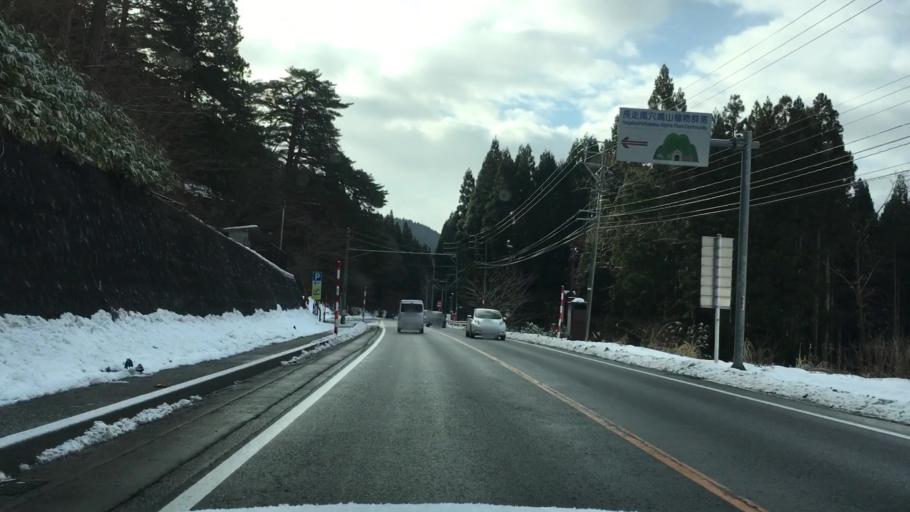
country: JP
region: Akita
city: Odate
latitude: 40.3826
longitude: 140.6034
